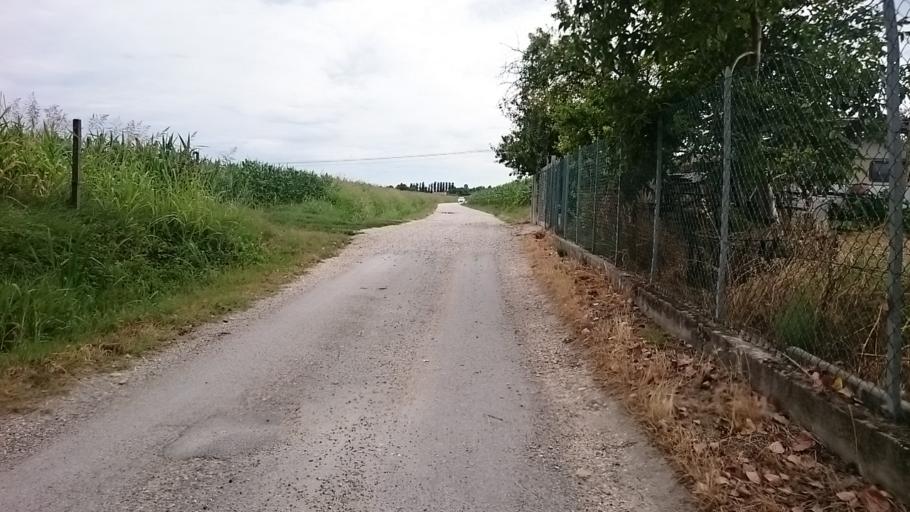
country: IT
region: Veneto
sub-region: Provincia di Padova
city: Albignasego
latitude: 45.3620
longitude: 11.8831
